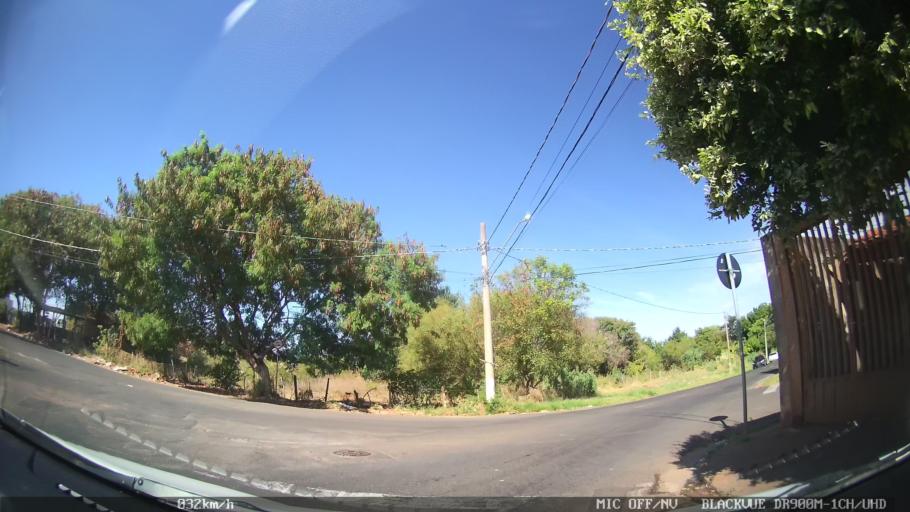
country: BR
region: Sao Paulo
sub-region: Sao Jose Do Rio Preto
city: Sao Jose do Rio Preto
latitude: -20.7693
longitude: -49.3982
